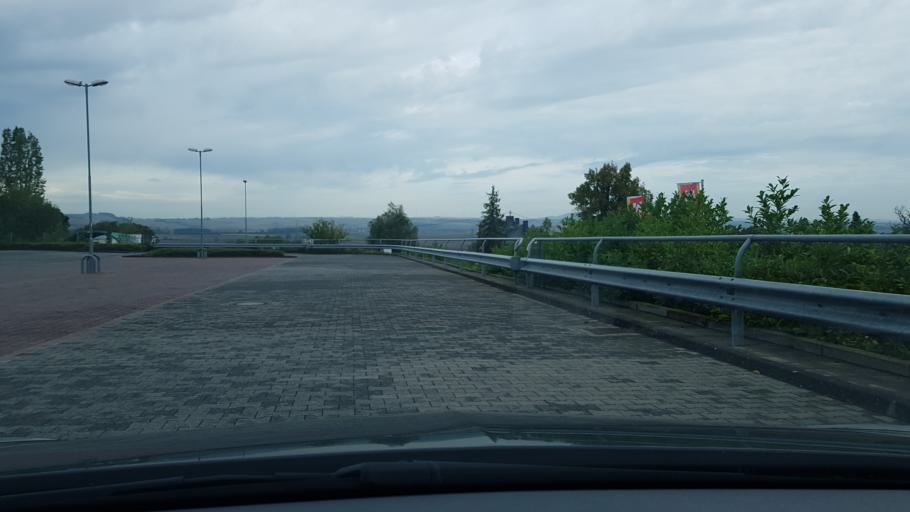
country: DE
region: Rheinland-Pfalz
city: Munstermaifeld
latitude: 50.2502
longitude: 7.3566
